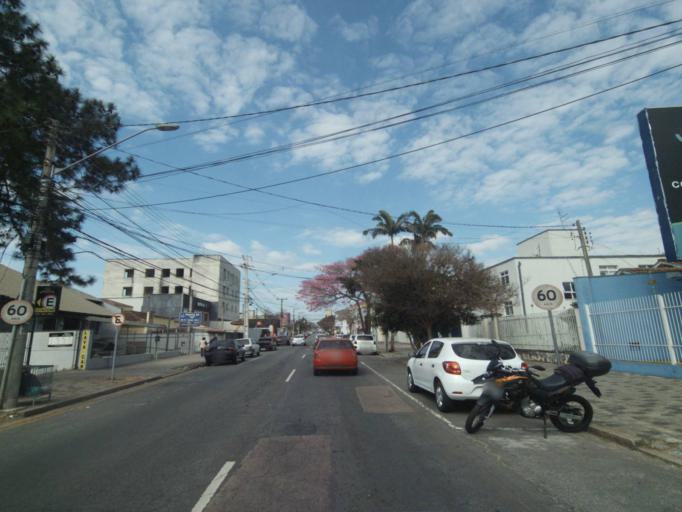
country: BR
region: Parana
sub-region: Curitiba
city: Curitiba
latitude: -25.4487
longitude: -49.2714
